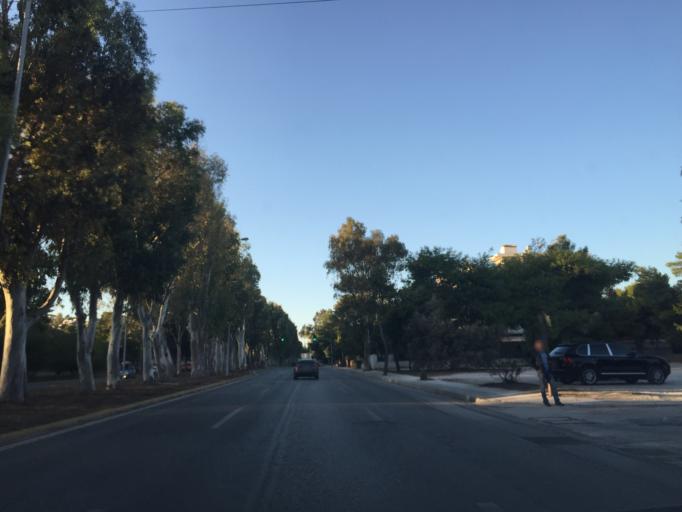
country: GR
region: Attica
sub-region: Nomarchia Anatolikis Attikis
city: Vouliagmeni
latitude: 37.8172
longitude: 23.7779
